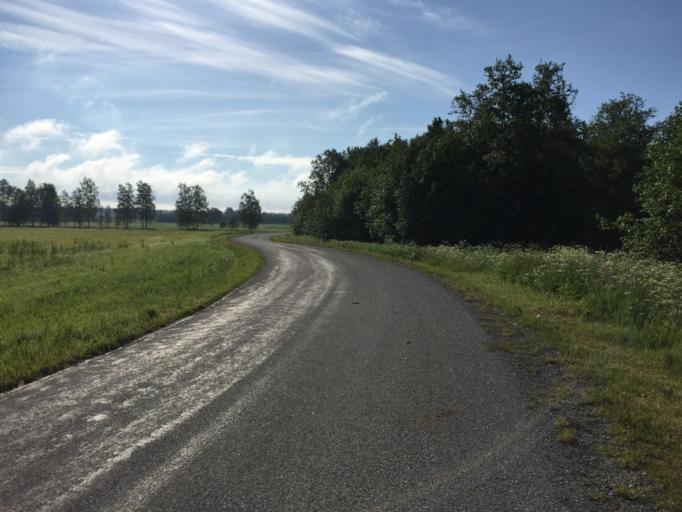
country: EE
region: Jogevamaa
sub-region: Mustvee linn
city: Mustvee
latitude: 59.0004
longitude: 26.9412
